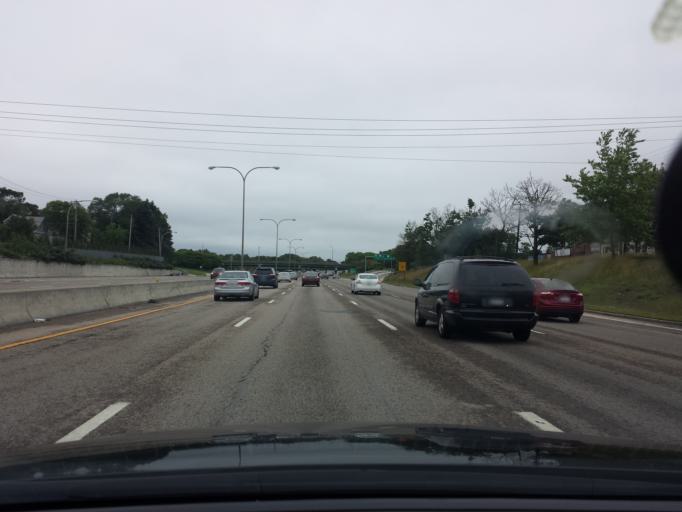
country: US
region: Rhode Island
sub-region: Providence County
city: Cranston
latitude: 41.7780
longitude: -71.4257
